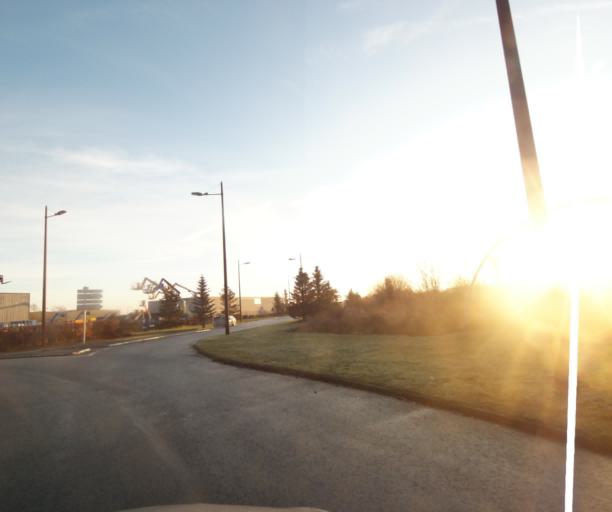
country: FR
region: Nord-Pas-de-Calais
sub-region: Departement du Nord
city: Quarouble
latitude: 50.3793
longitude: 3.6151
